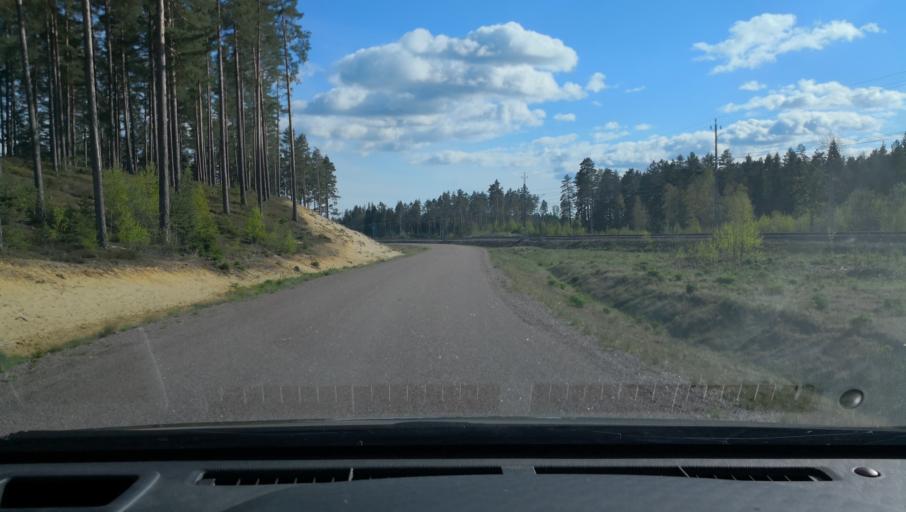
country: SE
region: OErebro
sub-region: Askersunds Kommun
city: Asbro
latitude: 58.9458
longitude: 15.0415
